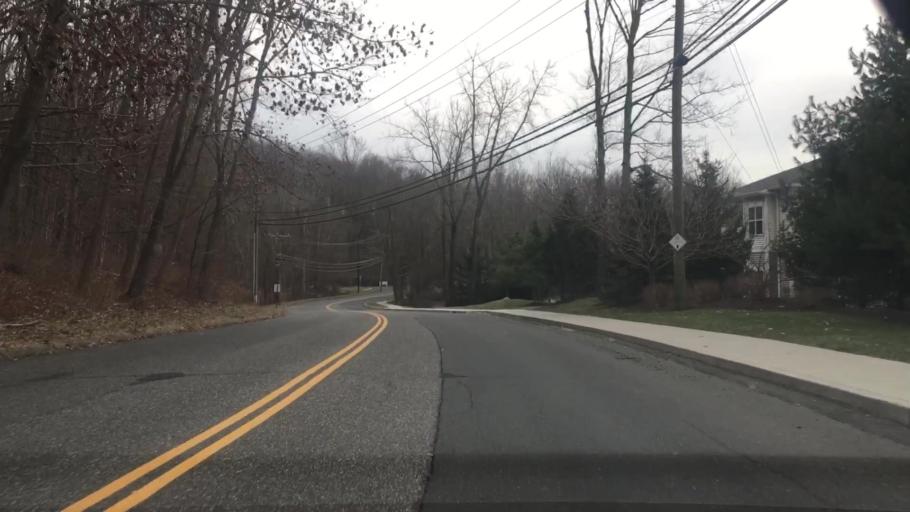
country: US
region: New York
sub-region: Putnam County
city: Peach Lake
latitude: 41.3796
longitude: -73.5347
